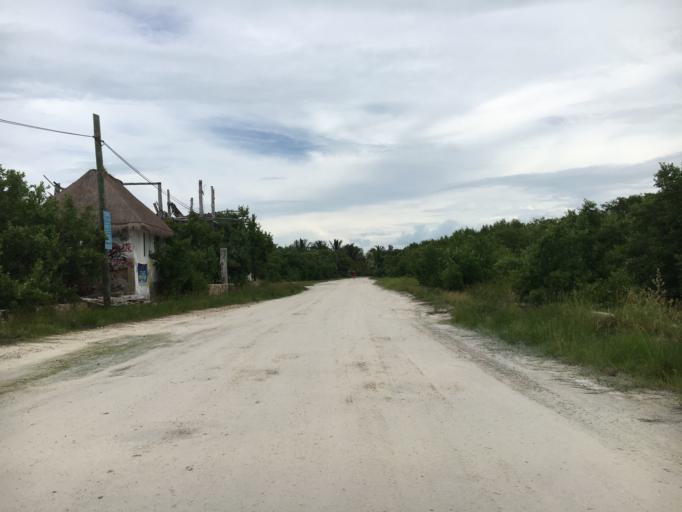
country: MX
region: Quintana Roo
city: Kantunilkin
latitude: 21.5331
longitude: -87.3652
